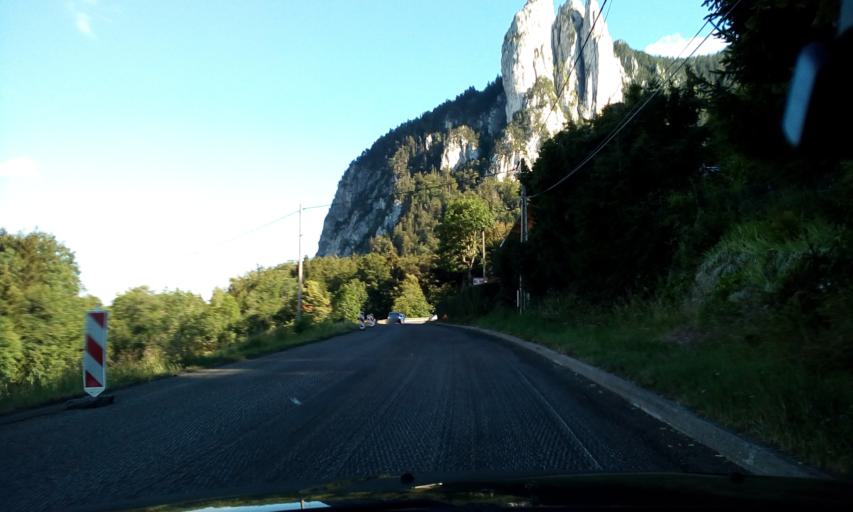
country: FR
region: Rhone-Alpes
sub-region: Departement de l'Isere
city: Seyssins
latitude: 45.1699
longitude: 5.6390
